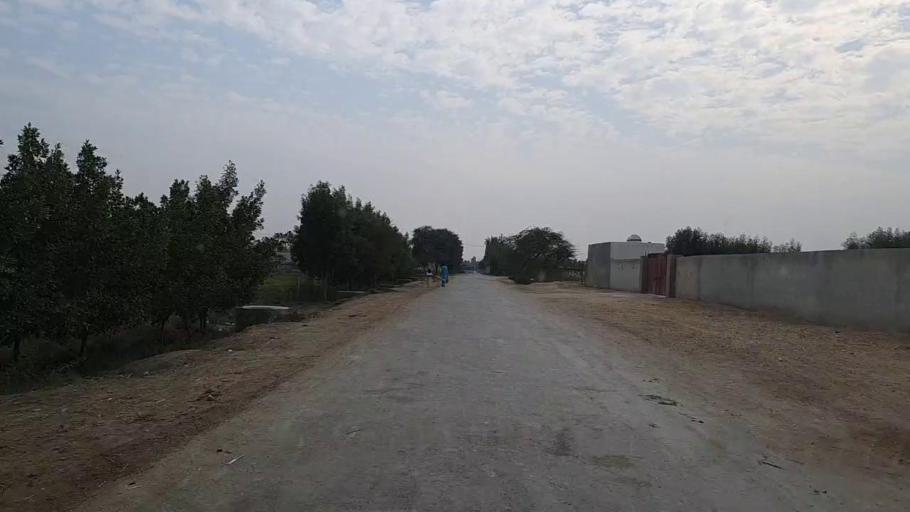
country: PK
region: Sindh
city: Mirwah Gorchani
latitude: 25.3729
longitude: 69.0817
